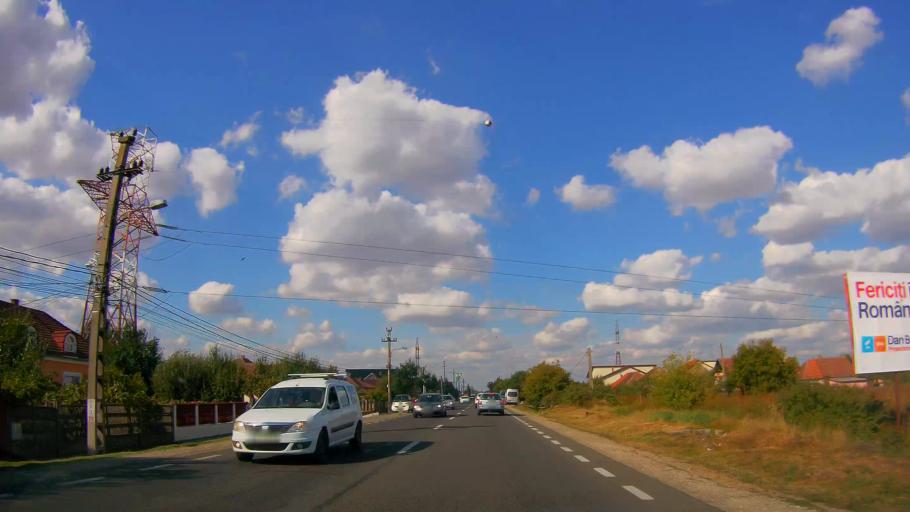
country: RO
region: Satu Mare
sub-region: Municipiul Satu Mare
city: Satu Mare
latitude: 47.7596
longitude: 22.8833
